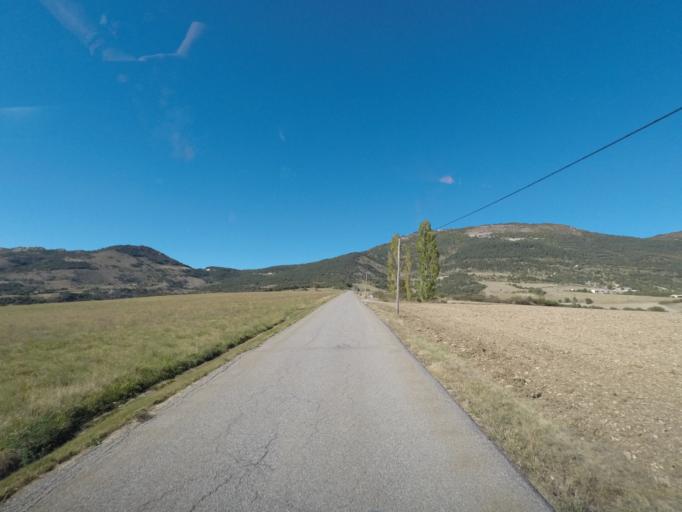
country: FR
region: Provence-Alpes-Cote d'Azur
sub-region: Departement des Hautes-Alpes
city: Serres
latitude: 44.4192
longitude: 5.5835
